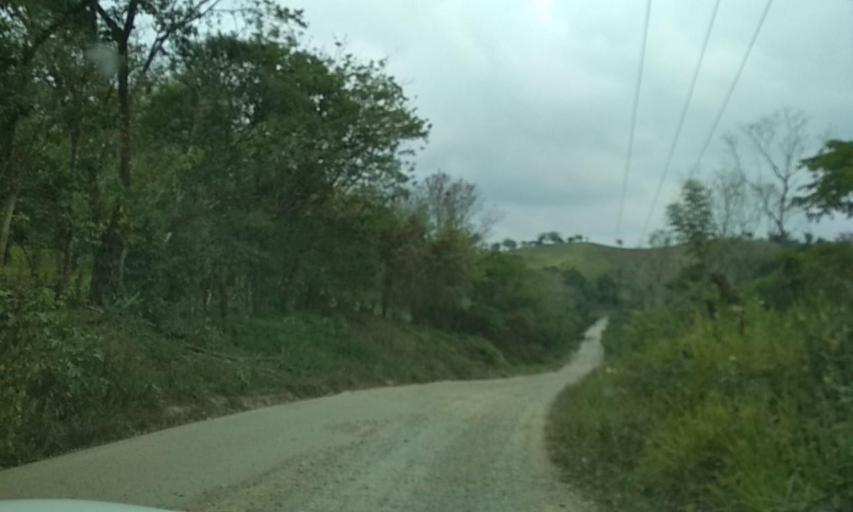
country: MX
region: Veracruz
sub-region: Uxpanapa
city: Poblado 10
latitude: 17.4949
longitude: -94.1365
